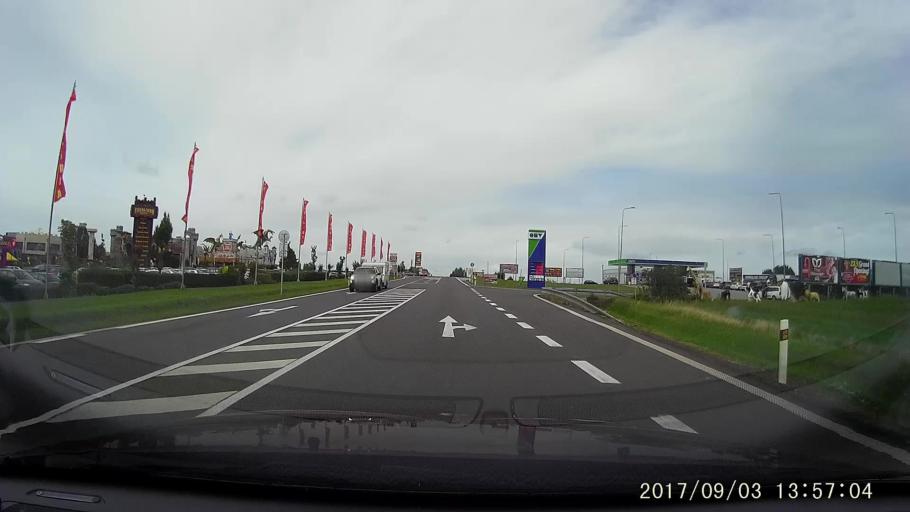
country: CZ
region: South Moravian
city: Vrbovec
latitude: 48.7640
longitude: 16.0661
